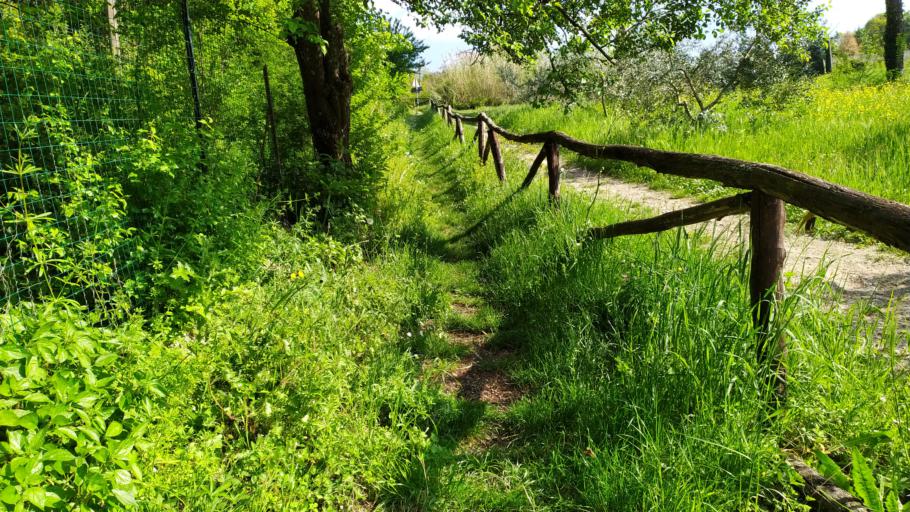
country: IT
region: Emilia-Romagna
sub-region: Provincia di Bologna
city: Borgo Tossignano
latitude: 44.2746
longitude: 11.6004
